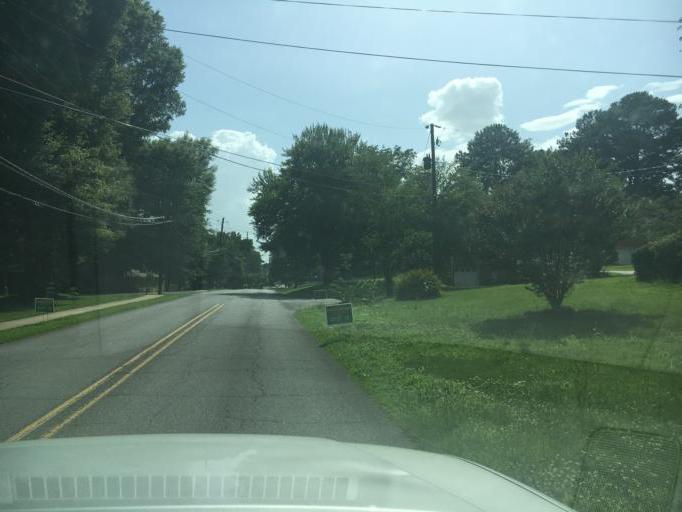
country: US
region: Alabama
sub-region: Jefferson County
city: Homewood
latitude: 33.4594
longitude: -86.8317
